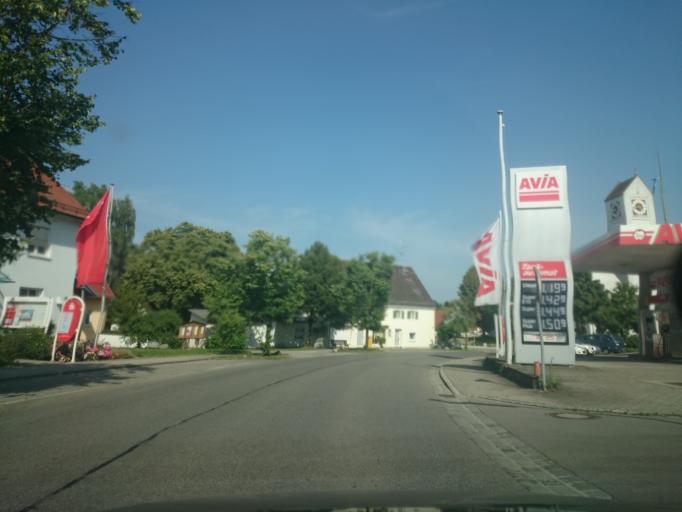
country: DE
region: Bavaria
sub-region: Upper Bavaria
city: Althegnenberg
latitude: 48.2346
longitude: 11.0626
